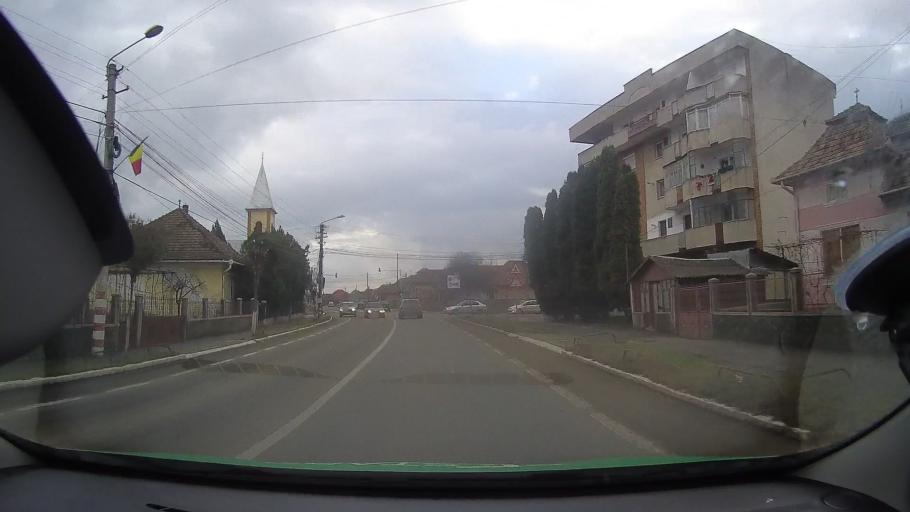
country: RO
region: Cluj
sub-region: Municipiul Campia Turzii
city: Campia Turzii
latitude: 46.5355
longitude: 23.8955
